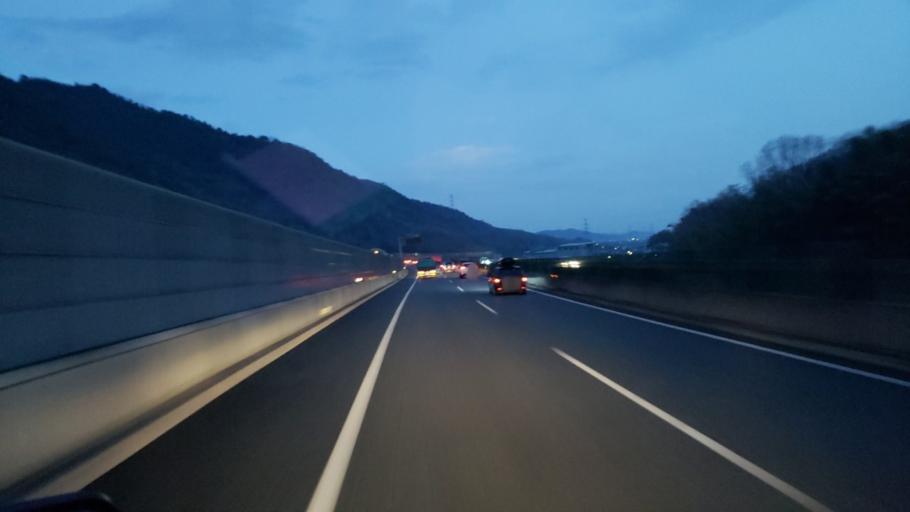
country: JP
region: Hyogo
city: Kakogawacho-honmachi
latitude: 34.8493
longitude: 134.8099
